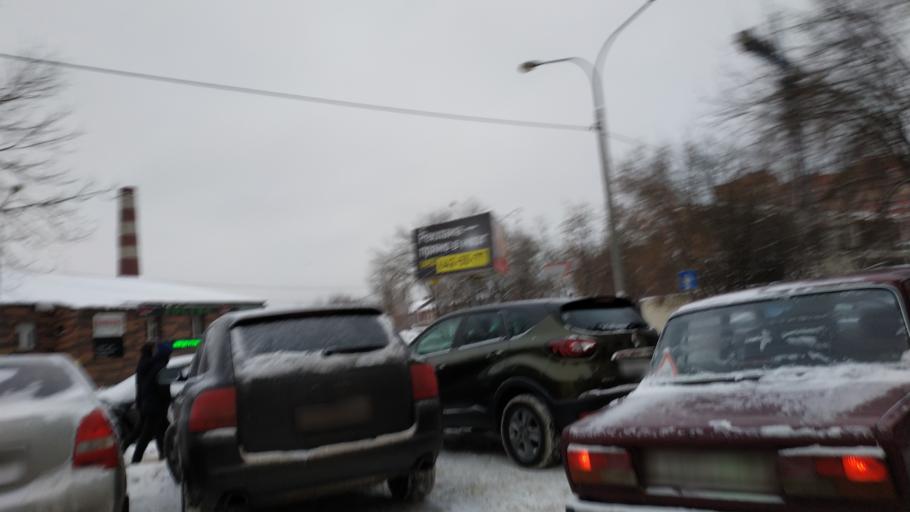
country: RU
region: Moskovskaya
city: Shchelkovo
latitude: 55.9270
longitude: 37.9904
